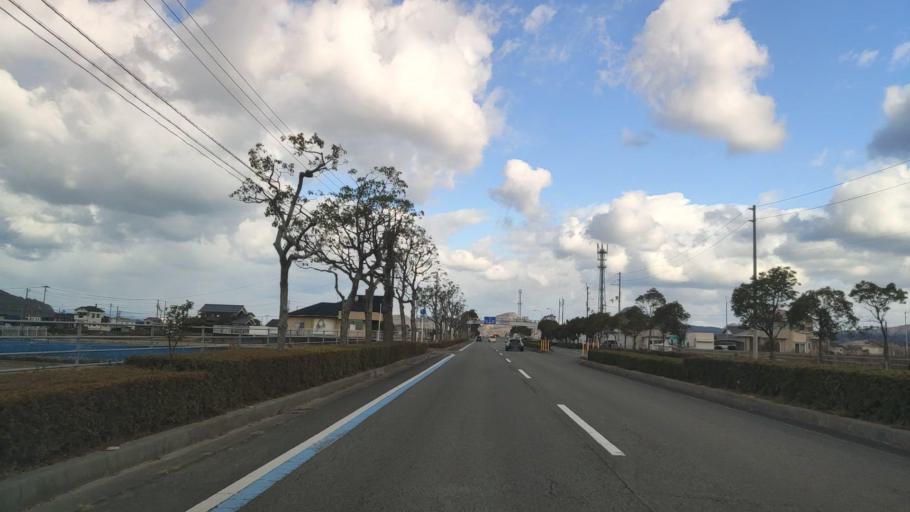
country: JP
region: Ehime
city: Hojo
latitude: 33.9516
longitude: 132.7747
